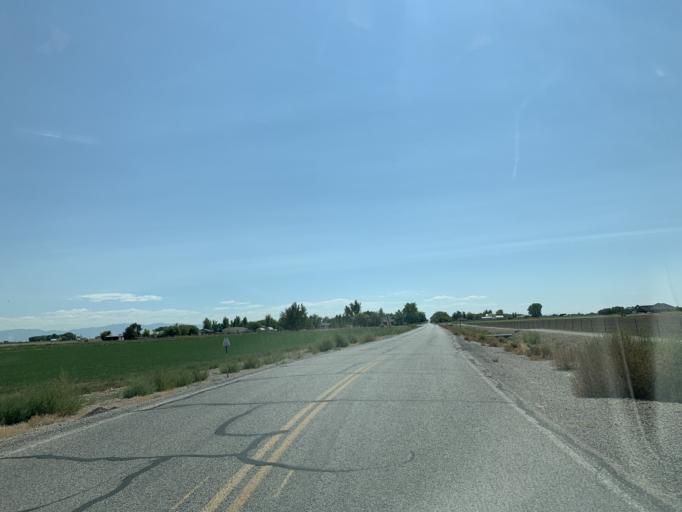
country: US
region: Utah
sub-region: Millard County
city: Delta
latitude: 39.3403
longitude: -112.6147
